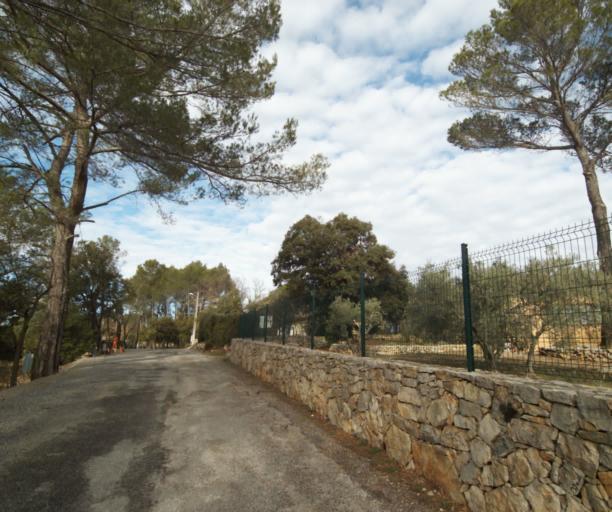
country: FR
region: Provence-Alpes-Cote d'Azur
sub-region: Departement du Var
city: Trans-en-Provence
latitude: 43.5049
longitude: 6.4783
